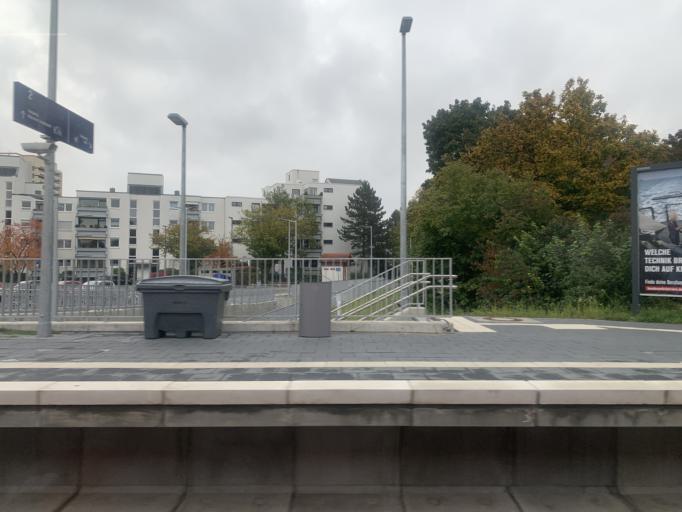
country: DE
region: Bavaria
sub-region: Upper Bavaria
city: Unterschleissheim
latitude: 48.2747
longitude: 11.5693
